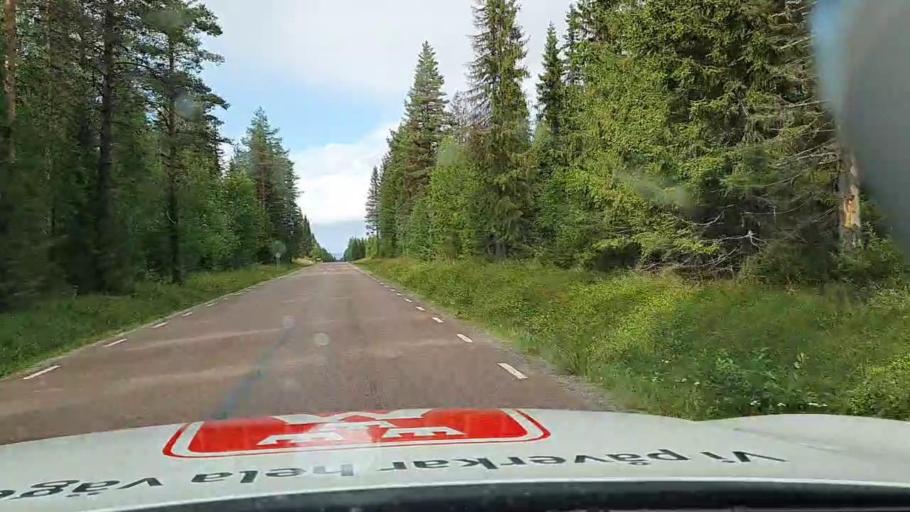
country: SE
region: Jaemtland
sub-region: Stroemsunds Kommun
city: Stroemsund
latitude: 63.8694
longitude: 15.3723
